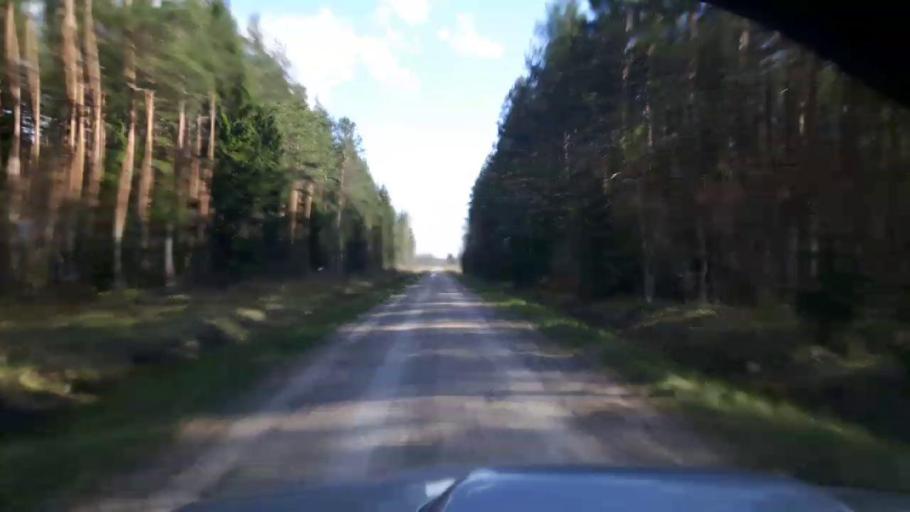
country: EE
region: Paernumaa
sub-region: Tootsi vald
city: Tootsi
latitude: 58.4215
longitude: 24.8518
